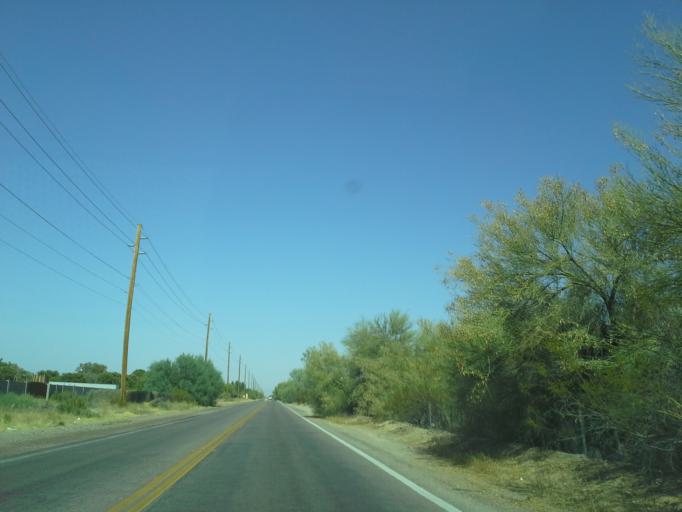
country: US
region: Arizona
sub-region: Maricopa County
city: Queen Creek
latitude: 33.2046
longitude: -111.6856
